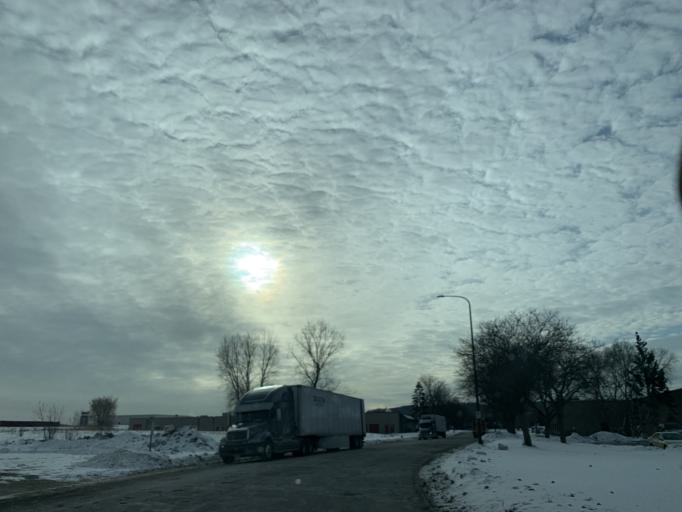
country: US
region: Minnesota
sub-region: Ramsey County
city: Saint Paul
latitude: 44.9392
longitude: -93.0721
